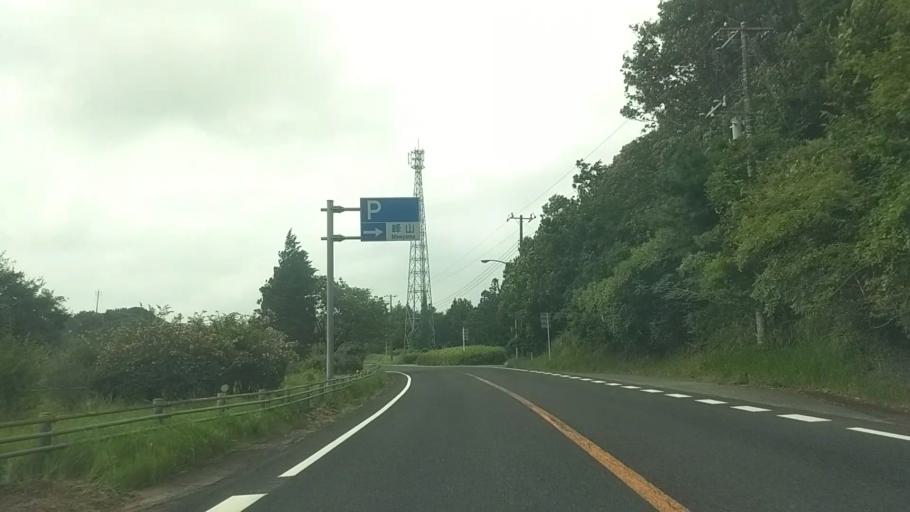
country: JP
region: Chiba
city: Kawaguchi
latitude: 35.2288
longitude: 140.0315
